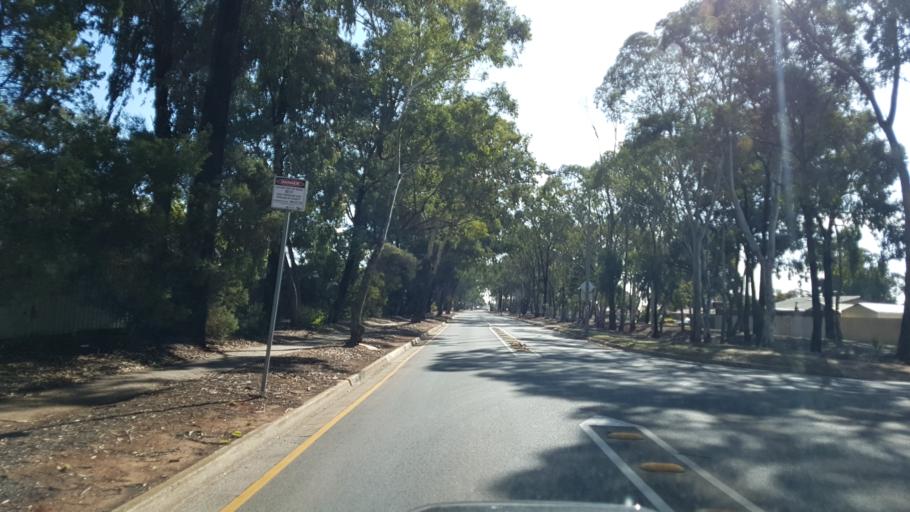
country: AU
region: South Australia
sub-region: Salisbury
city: Salisbury
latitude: -34.7373
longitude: 138.6217
